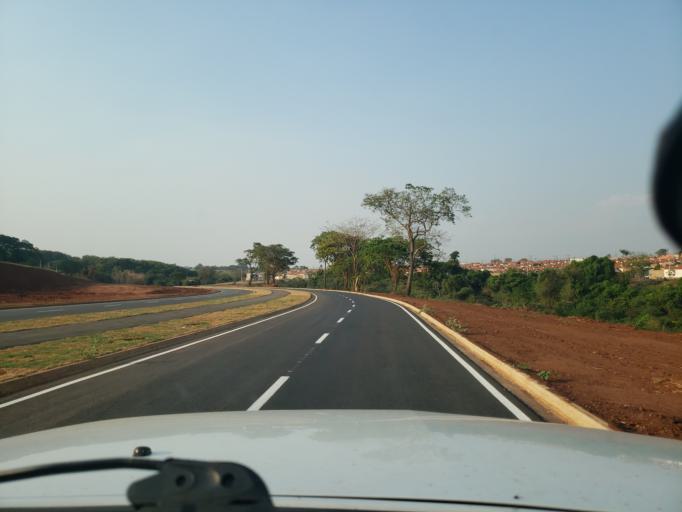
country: BR
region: Sao Paulo
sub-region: Moji-Guacu
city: Mogi-Gaucu
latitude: -22.3195
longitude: -46.9465
